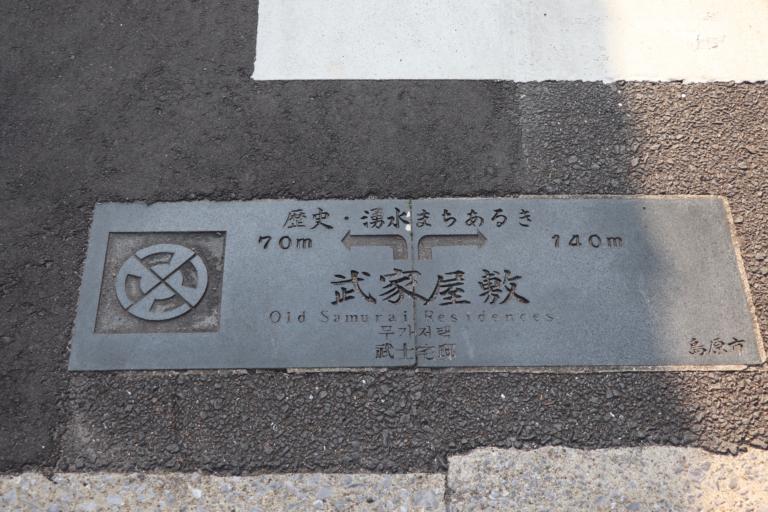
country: JP
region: Nagasaki
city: Shimabara
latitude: 32.7915
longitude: 130.3636
